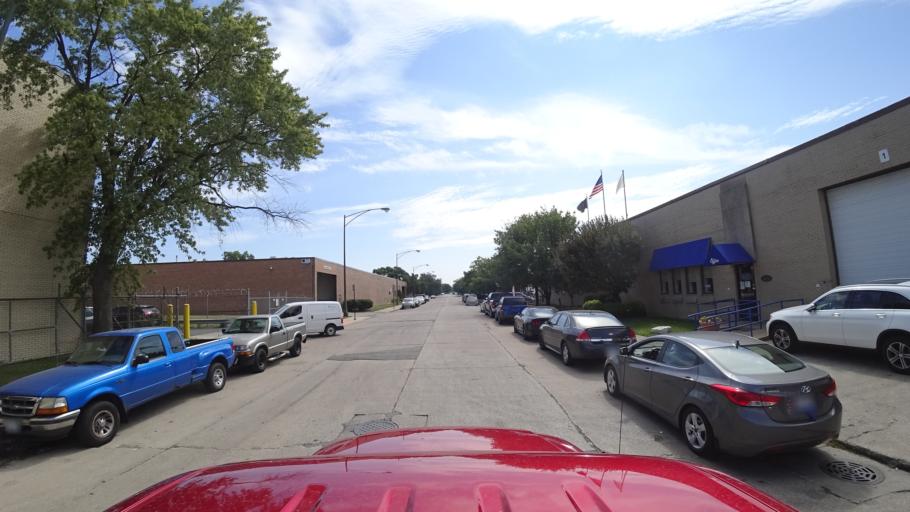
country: US
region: Illinois
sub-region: Cook County
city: Chicago
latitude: 41.8211
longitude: -87.6542
